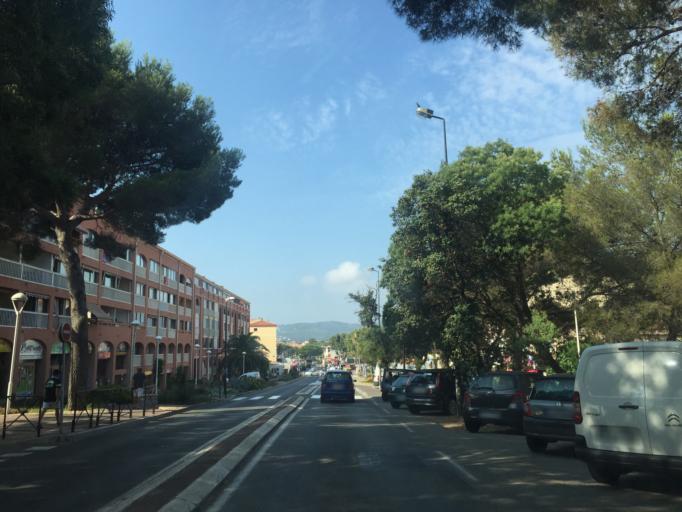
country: FR
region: Provence-Alpes-Cote d'Azur
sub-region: Departement du Var
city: Frejus
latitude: 43.3877
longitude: 6.7241
